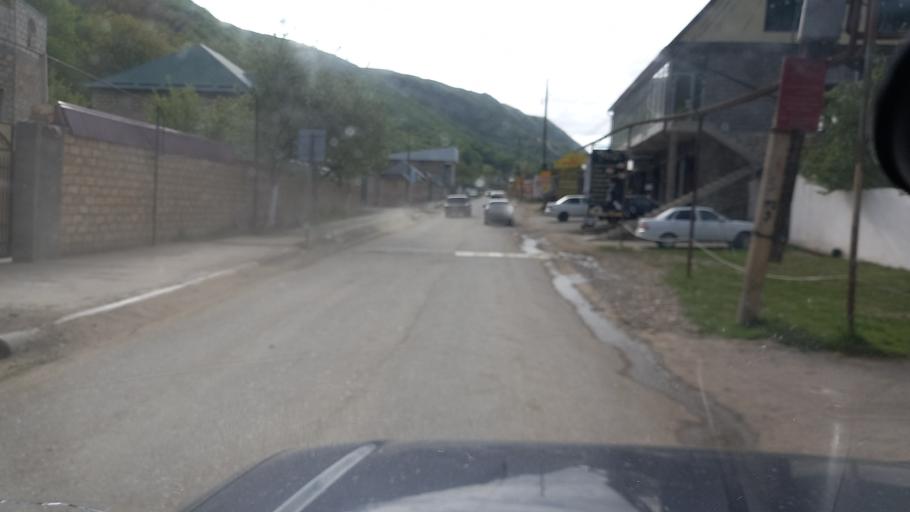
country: RU
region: Dagestan
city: Khuchni
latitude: 41.9624
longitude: 47.9548
